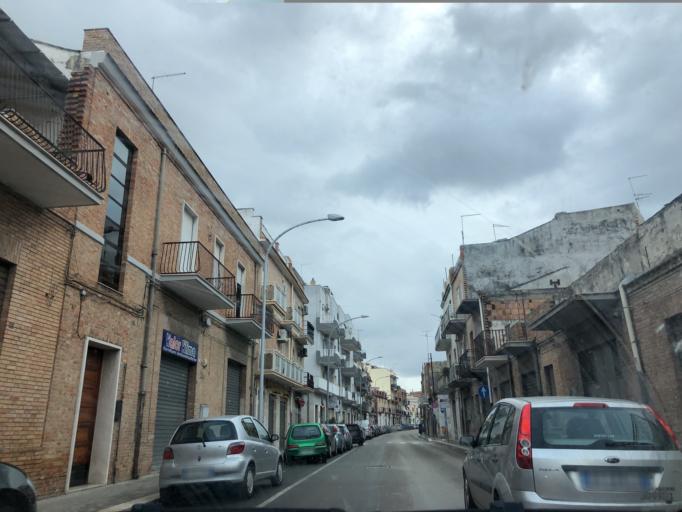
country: IT
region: Apulia
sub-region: Provincia di Foggia
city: Lucera
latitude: 41.5096
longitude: 15.3396
